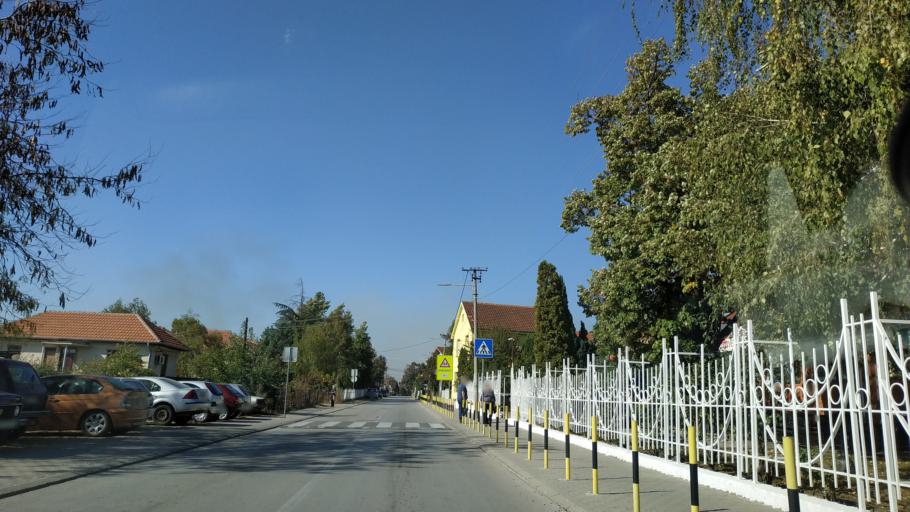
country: RS
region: Central Serbia
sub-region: Nisavski Okrug
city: Aleksinac
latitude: 43.5401
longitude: 21.6989
